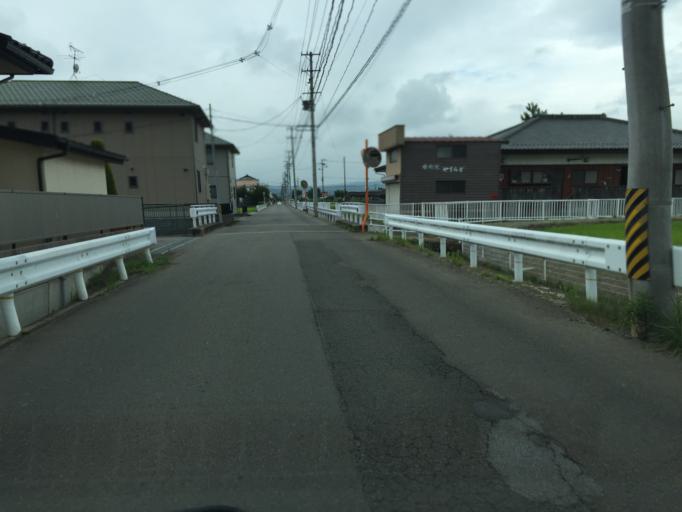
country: JP
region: Fukushima
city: Fukushima-shi
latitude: 37.7373
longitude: 140.4461
